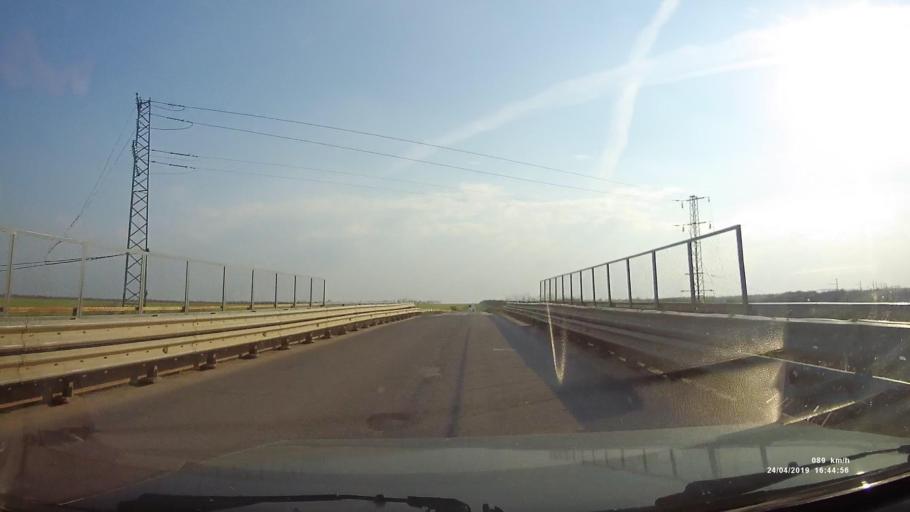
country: RU
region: Rostov
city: Gundorovskiy
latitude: 46.7756
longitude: 41.8206
